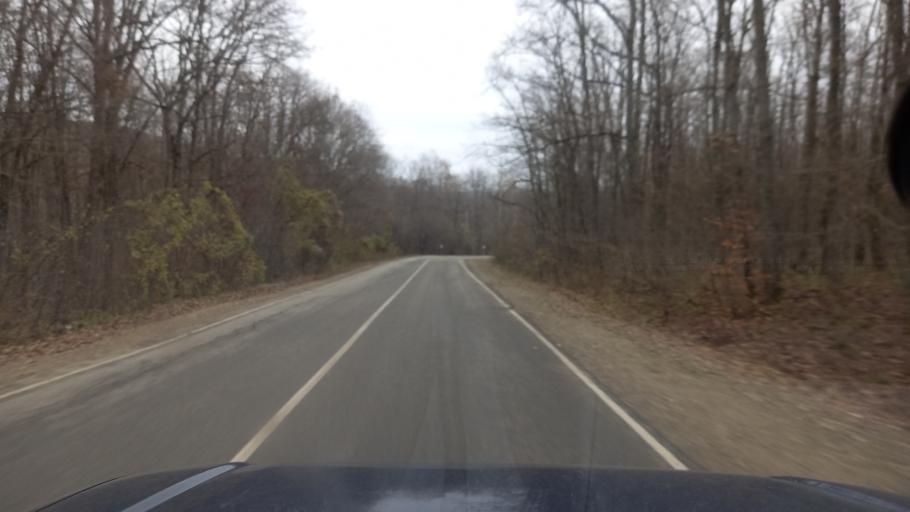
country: RU
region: Krasnodarskiy
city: Goryachiy Klyuch
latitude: 44.5436
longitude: 39.2640
